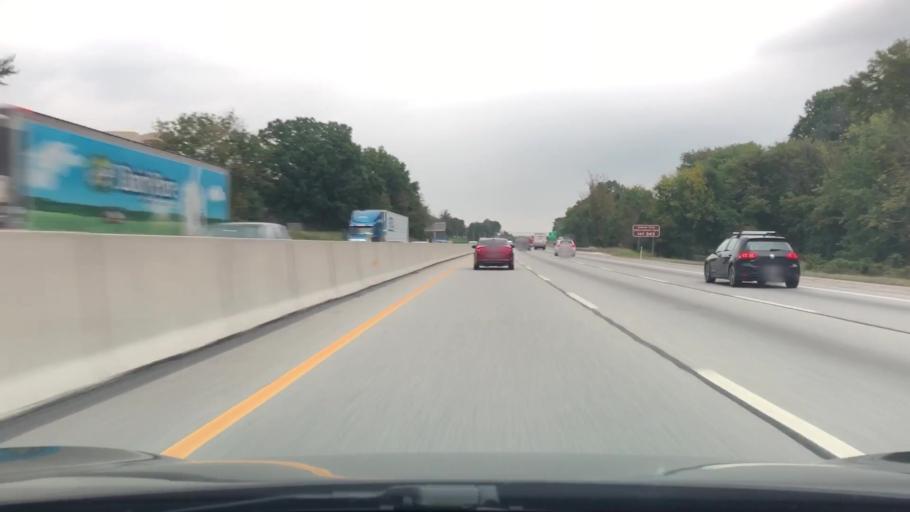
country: US
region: Pennsylvania
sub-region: Montgomery County
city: Dresher
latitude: 40.1506
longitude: -75.1465
